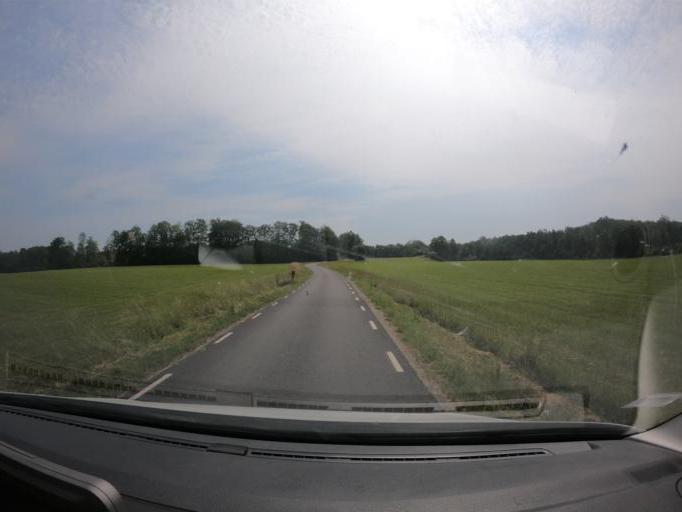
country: SE
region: Skane
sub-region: Hassleholms Kommun
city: Bjarnum
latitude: 56.2494
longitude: 13.6940
